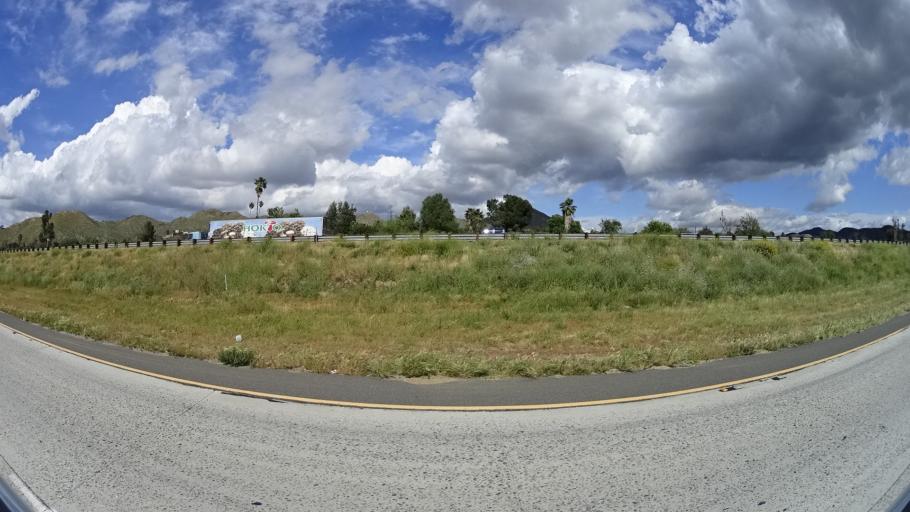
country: US
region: California
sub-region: Riverside County
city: Sedco Hills
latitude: 33.6293
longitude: -117.2750
